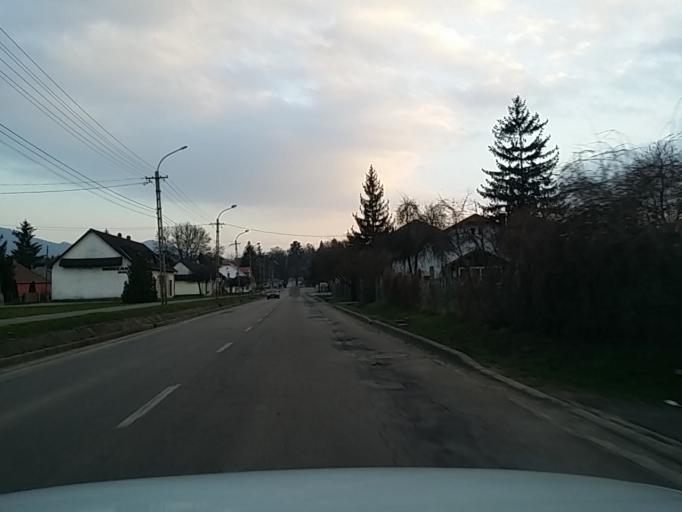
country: HU
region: Nograd
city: Batonyterenye
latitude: 47.9795
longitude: 19.8217
